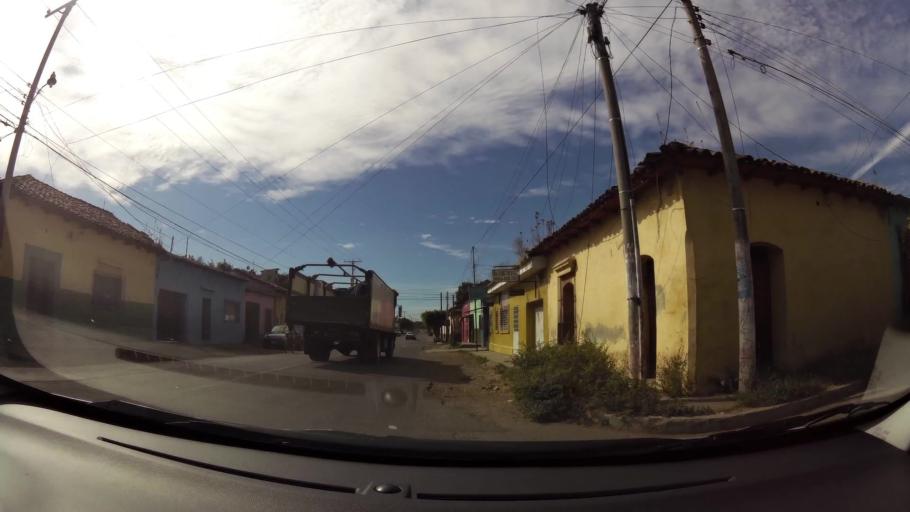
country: SV
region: Santa Ana
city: Chalchuapa
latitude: 13.9811
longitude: -89.6783
